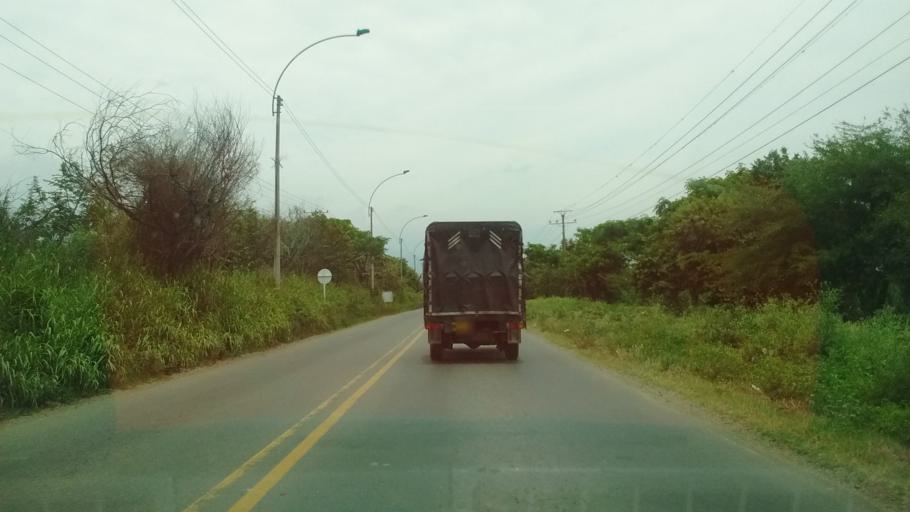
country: CO
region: Valle del Cauca
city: Jamundi
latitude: 3.3239
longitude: -76.5002
